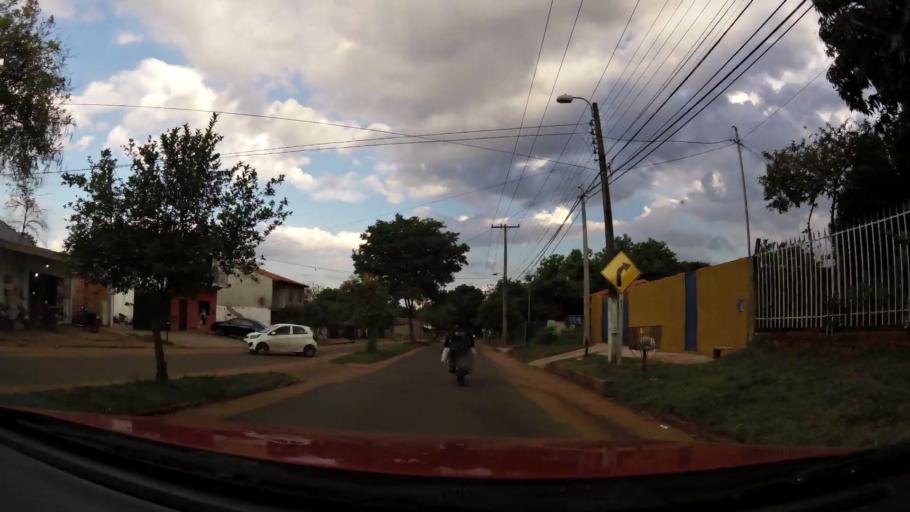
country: PY
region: Central
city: Nemby
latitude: -25.3717
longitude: -57.5494
